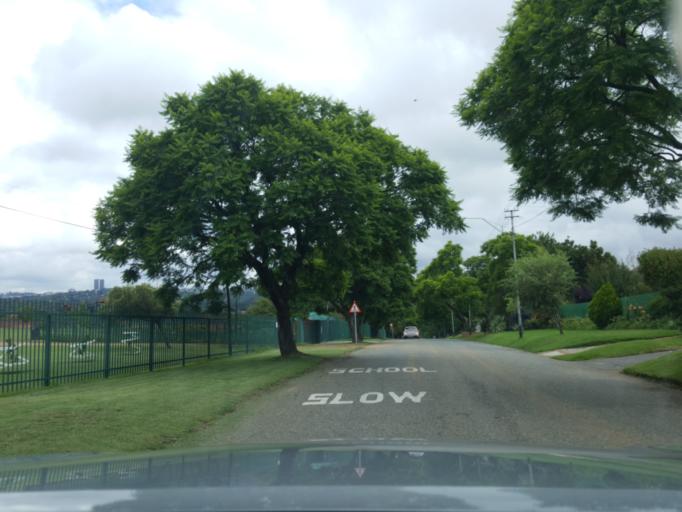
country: ZA
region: Gauteng
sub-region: City of Johannesburg Metropolitan Municipality
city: Johannesburg
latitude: -26.1357
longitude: 28.0034
